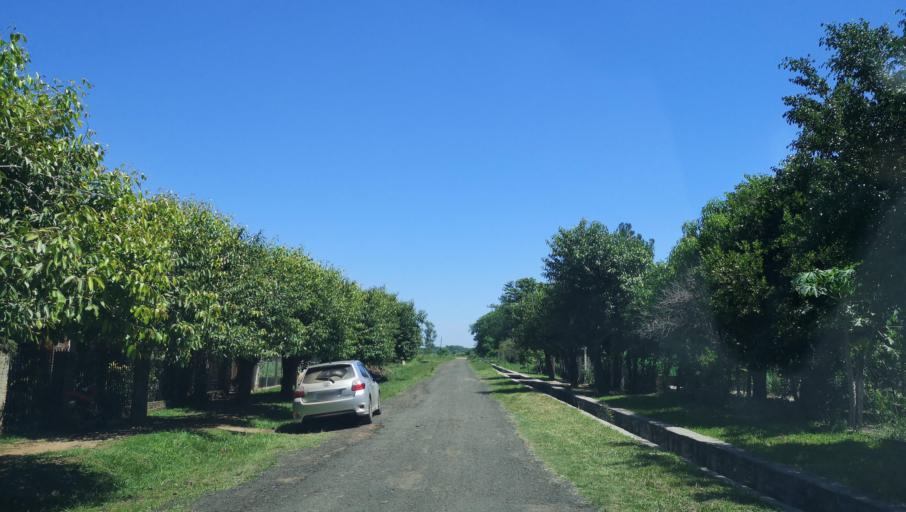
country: PY
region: Caaguazu
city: Carayao
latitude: -25.1980
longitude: -56.4016
